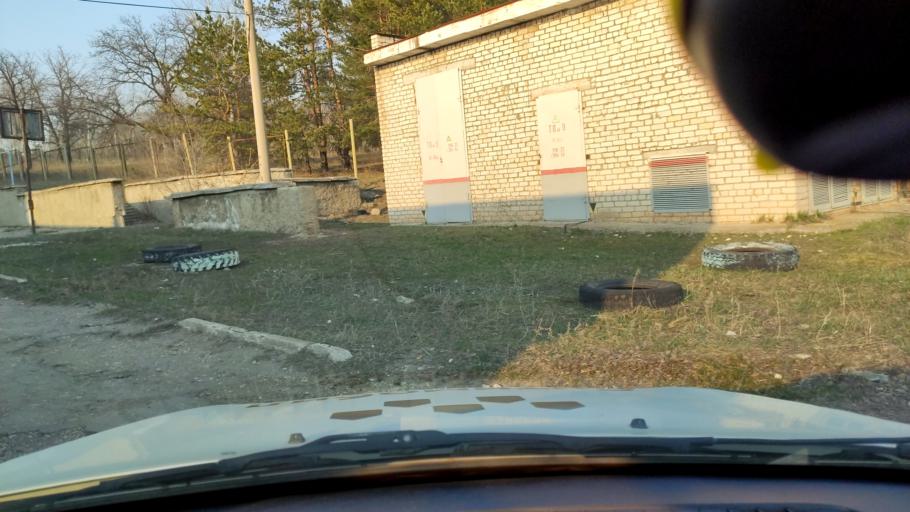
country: RU
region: Samara
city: Zhigulevsk
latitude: 53.4769
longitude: 49.5391
